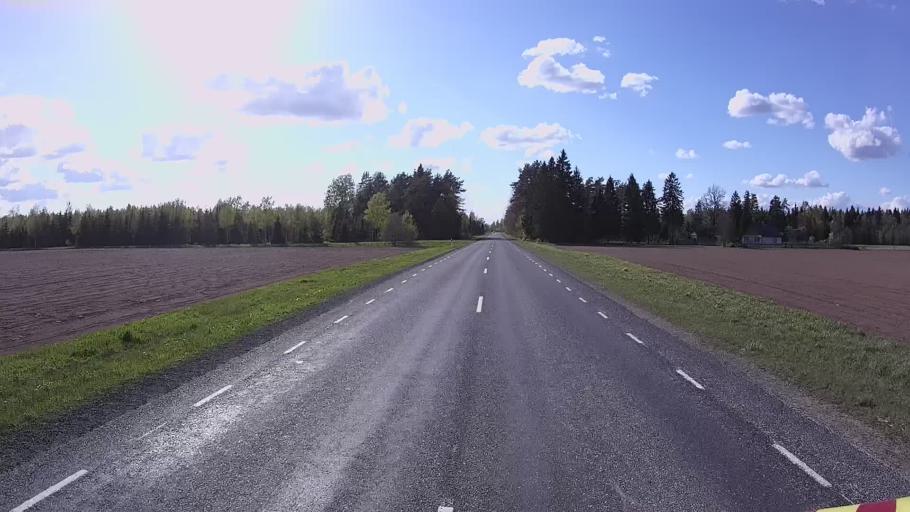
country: EE
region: Jogevamaa
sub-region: Jogeva linn
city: Jogeva
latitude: 58.7378
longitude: 26.2686
